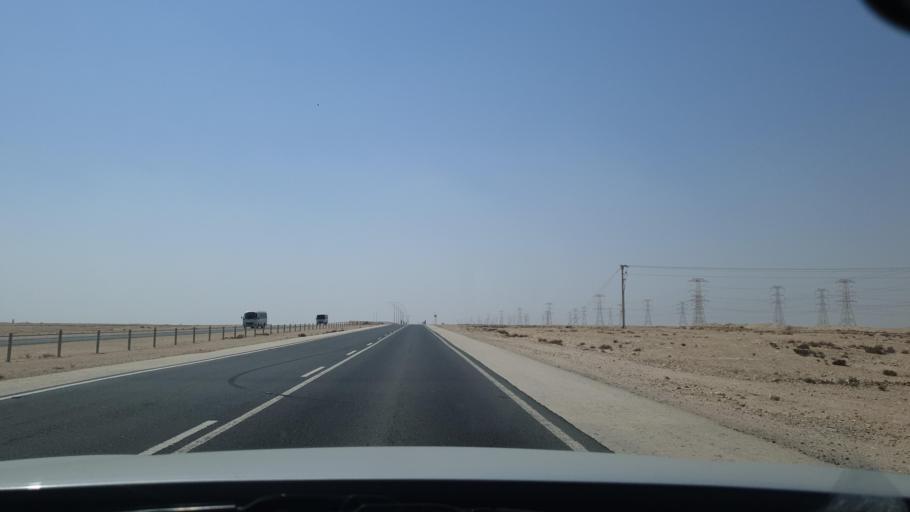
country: QA
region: Al Khawr
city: Al Khawr
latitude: 25.7379
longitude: 51.4598
